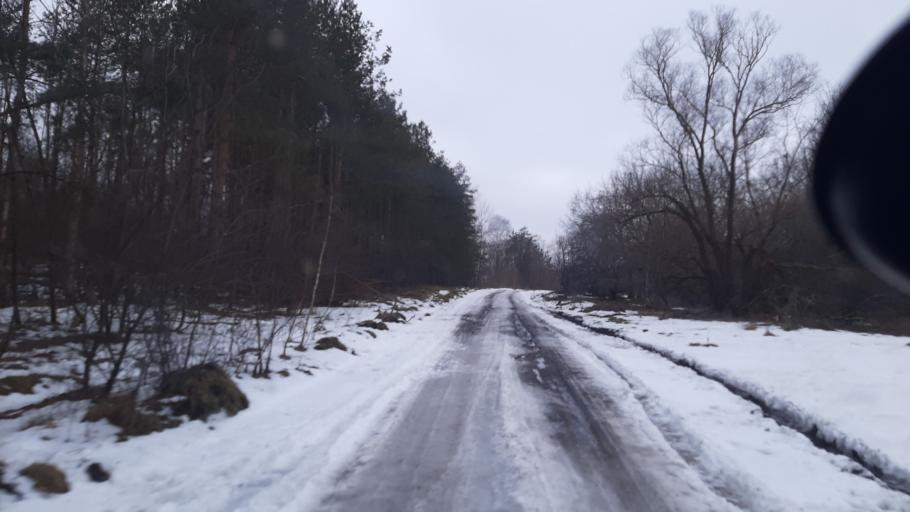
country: PL
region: Lublin Voivodeship
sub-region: Powiat wlodawski
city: Wlodawa
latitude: 51.5175
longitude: 23.5944
